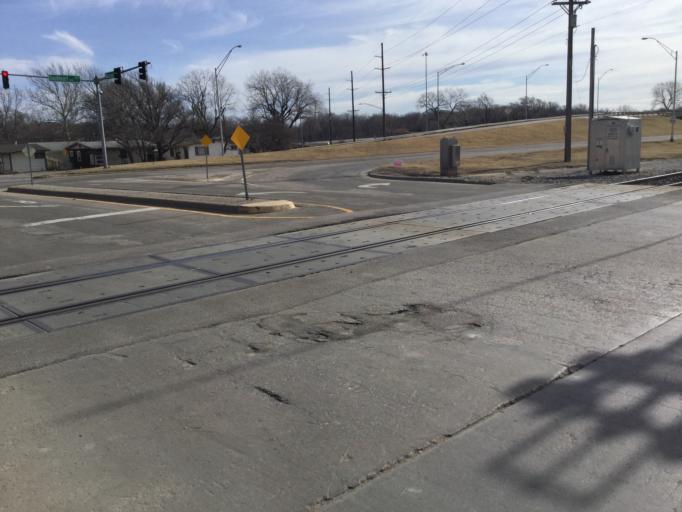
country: US
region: Kansas
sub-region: Sedgwick County
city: Wichita
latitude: 37.6425
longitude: -97.3111
